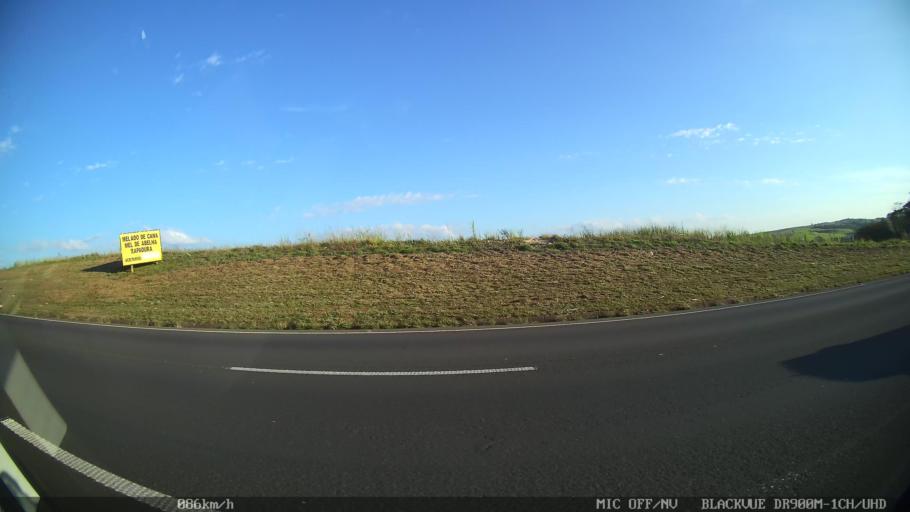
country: BR
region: Sao Paulo
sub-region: Santa Barbara D'Oeste
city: Santa Barbara d'Oeste
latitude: -22.7575
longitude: -47.4727
